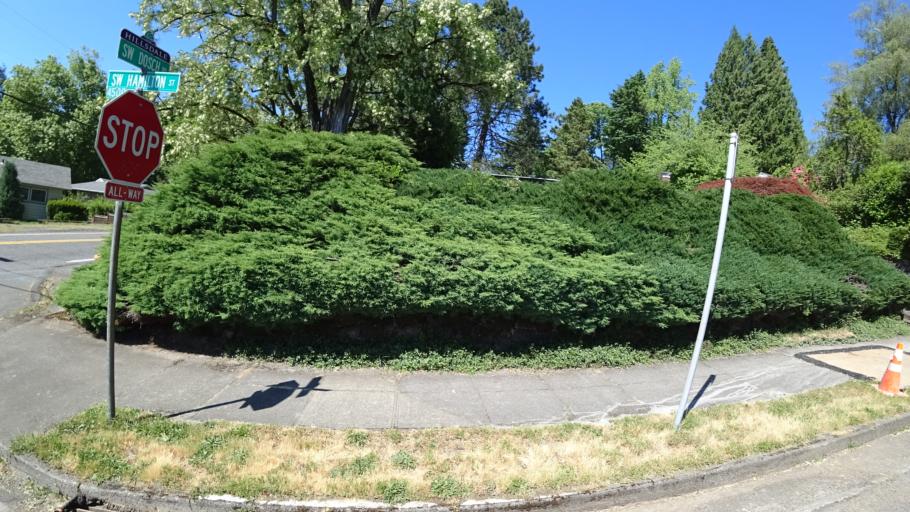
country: US
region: Oregon
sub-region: Multnomah County
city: Portland
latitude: 45.4906
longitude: -122.7102
